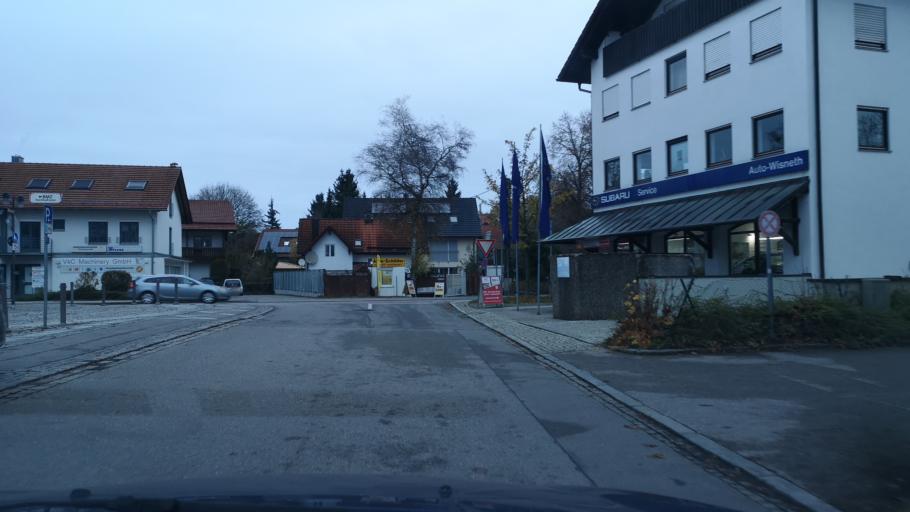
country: DE
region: Bavaria
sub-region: Upper Bavaria
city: Ebersberg
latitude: 48.0744
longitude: 11.9654
